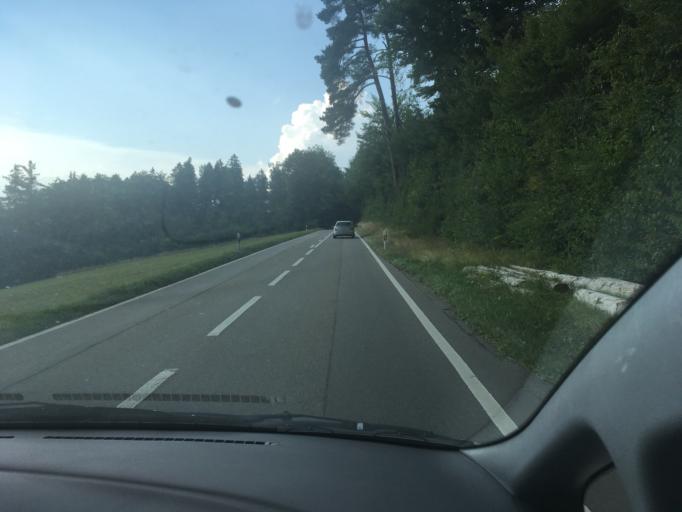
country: CH
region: Bern
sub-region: Bern-Mittelland District
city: Kirchlindach
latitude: 47.0023
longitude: 7.3856
